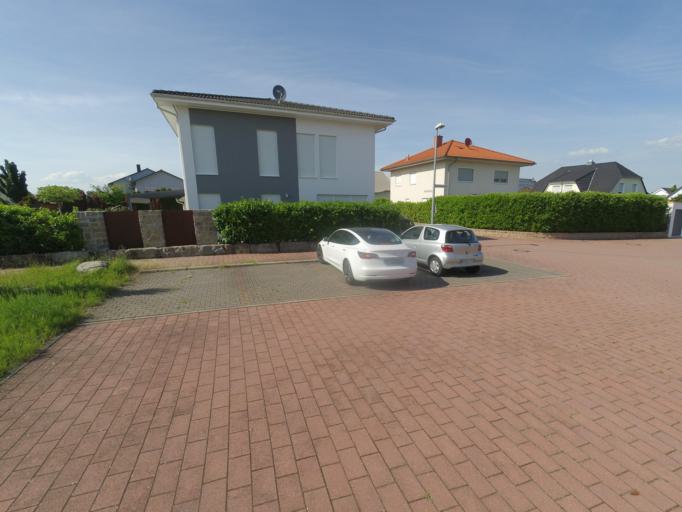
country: DE
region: Hesse
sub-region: Regierungsbezirk Darmstadt
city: Burstadt
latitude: 49.6375
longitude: 8.4758
